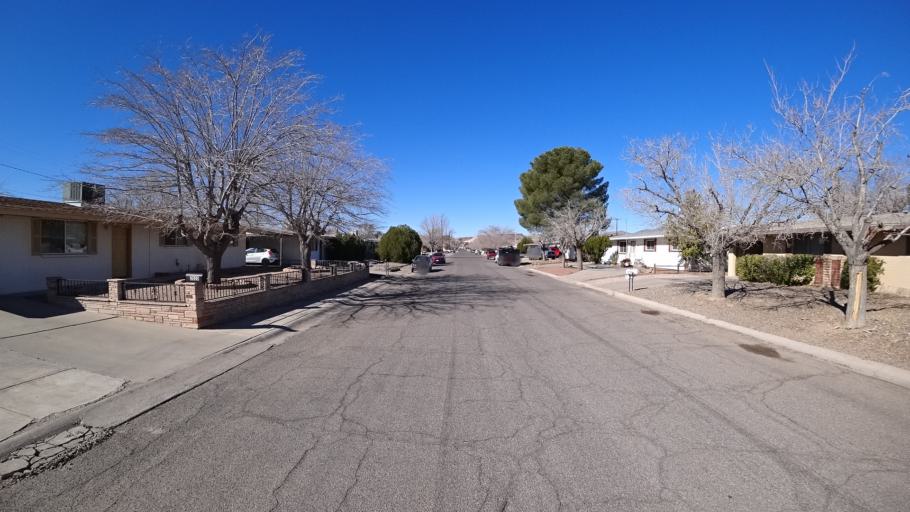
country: US
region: Arizona
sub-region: Mohave County
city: Kingman
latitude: 35.2096
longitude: -114.0303
